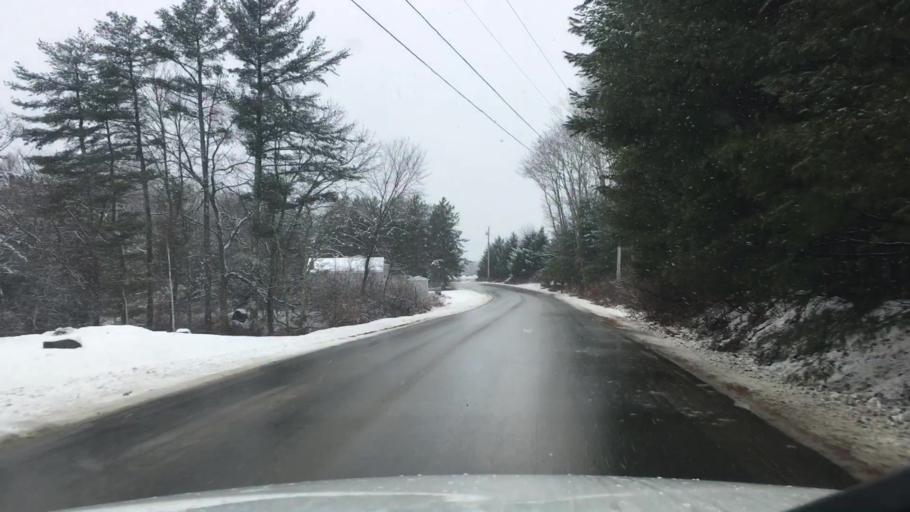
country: US
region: Maine
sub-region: Knox County
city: Union
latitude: 44.1564
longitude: -69.2915
